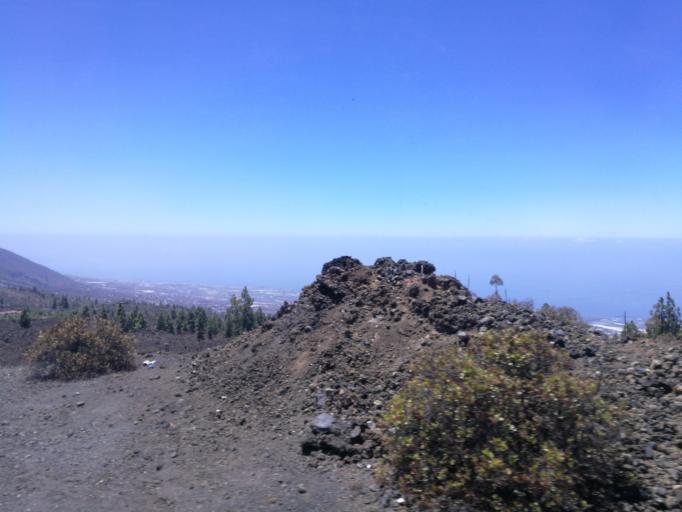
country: ES
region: Canary Islands
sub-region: Provincia de Santa Cruz de Tenerife
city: Guia de Isora
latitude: 28.2288
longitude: -16.7587
